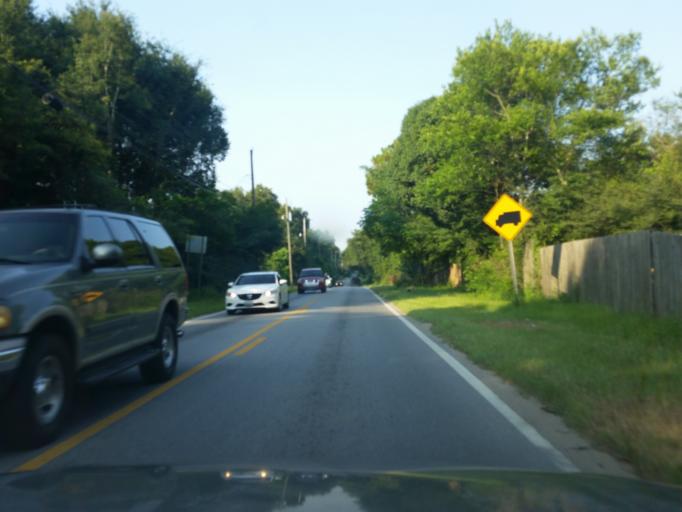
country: US
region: Florida
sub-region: Escambia County
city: Ensley
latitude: 30.4927
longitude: -87.2775
